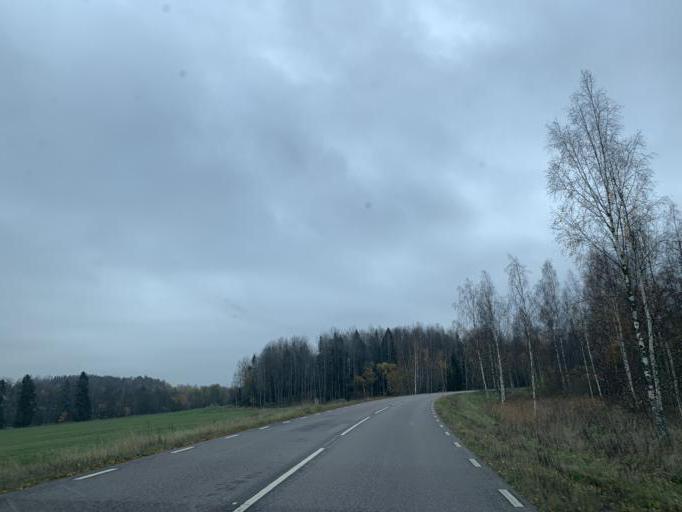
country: SE
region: Vaestmanland
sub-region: Surahammars Kommun
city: Ramnas
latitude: 59.7699
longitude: 16.1915
